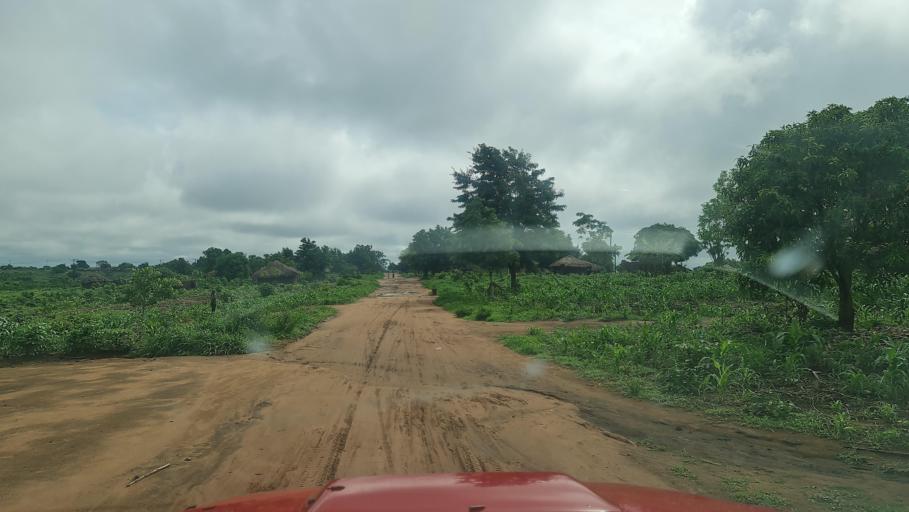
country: MW
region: Southern Region
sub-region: Nsanje District
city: Nsanje
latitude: -17.2217
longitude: 35.6688
